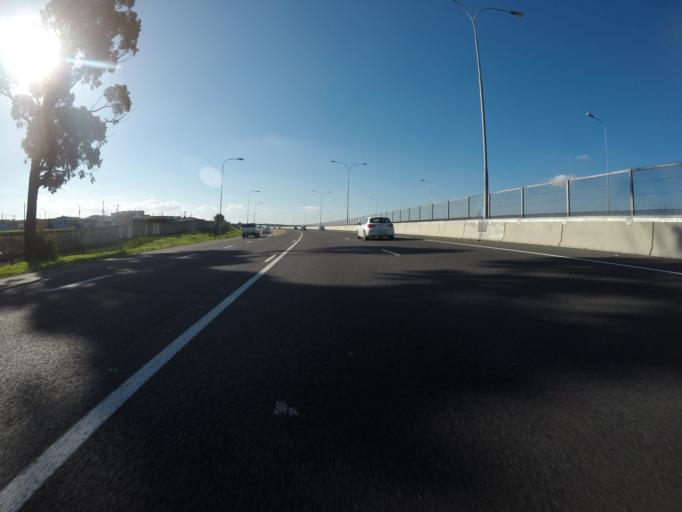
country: ZA
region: Western Cape
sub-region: City of Cape Town
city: Kraaifontein
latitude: -33.9831
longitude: 18.6510
